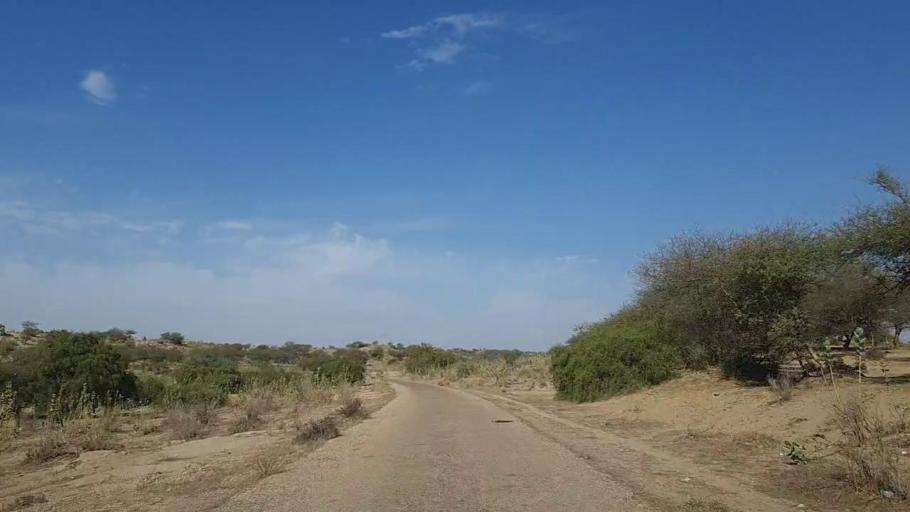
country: PK
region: Sindh
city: Naukot
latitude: 24.8384
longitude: 69.5511
